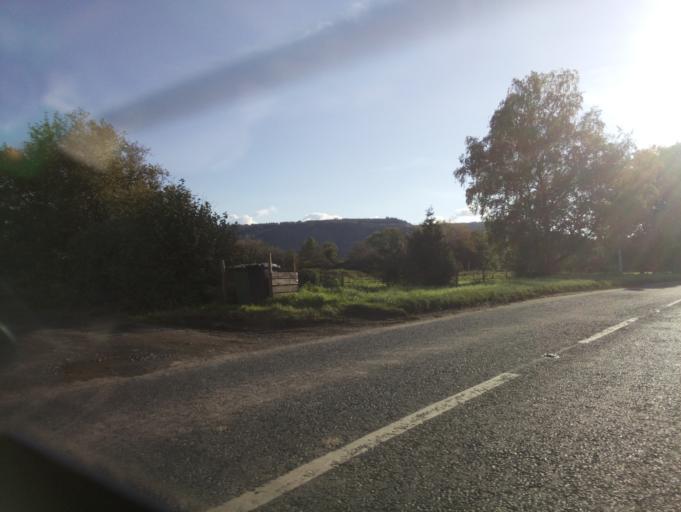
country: GB
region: England
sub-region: Herefordshire
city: Dorstone
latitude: 52.1207
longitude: -3.0044
